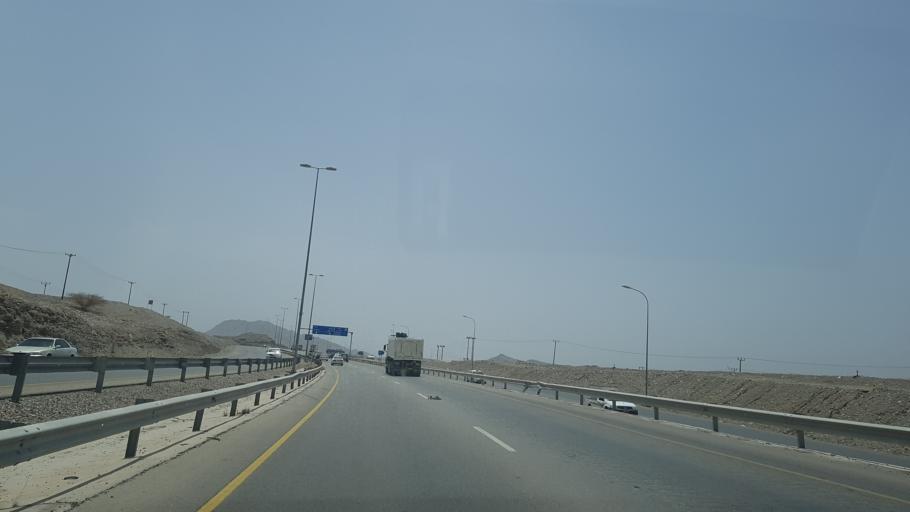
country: OM
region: Muhafazat ad Dakhiliyah
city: Bidbid
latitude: 23.4380
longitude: 58.1202
